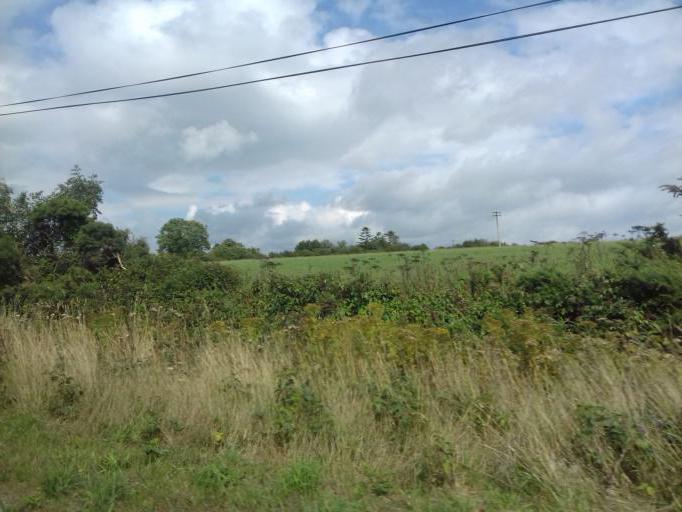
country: IE
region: Leinster
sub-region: Loch Garman
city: Loch Garman
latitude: 52.3034
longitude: -6.6452
